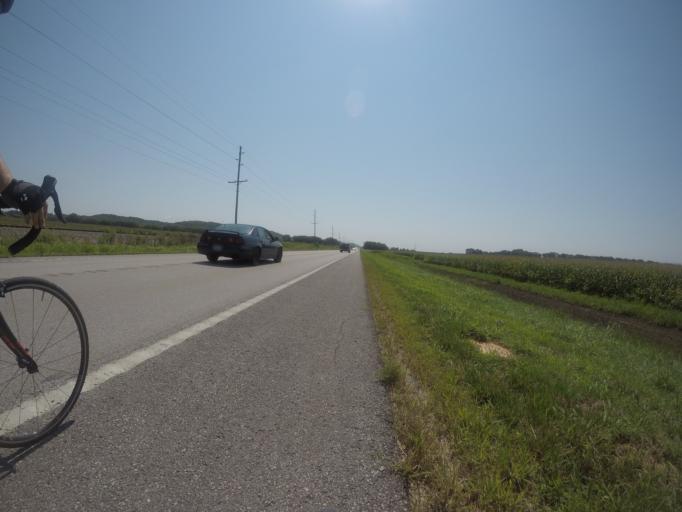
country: US
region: Kansas
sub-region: Atchison County
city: Atchison
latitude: 39.5263
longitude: -95.0313
